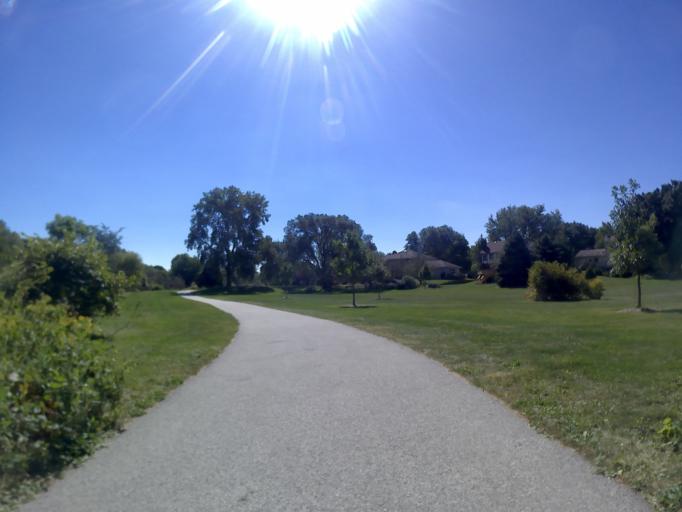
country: US
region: Illinois
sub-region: DuPage County
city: Naperville
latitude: 41.7784
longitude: -88.1702
